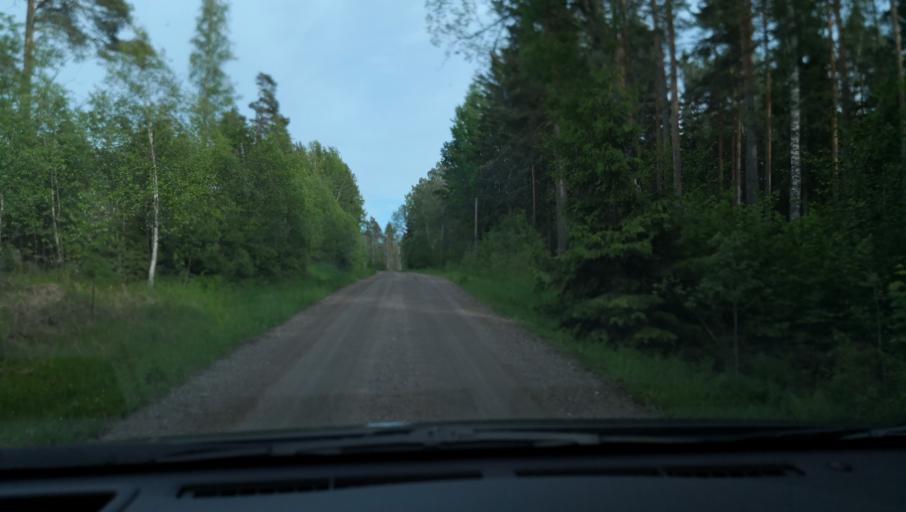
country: SE
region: Vaestmanland
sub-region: Arboga Kommun
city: Tyringe
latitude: 59.3639
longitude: 15.9573
